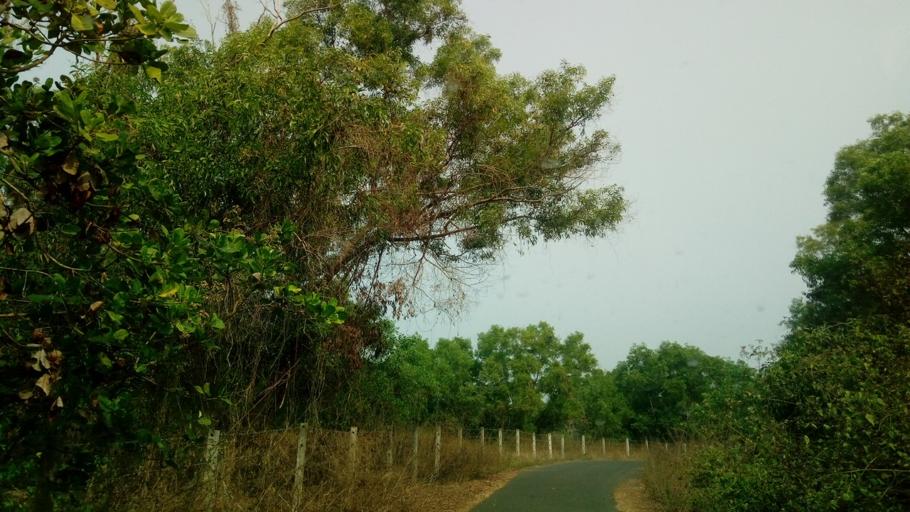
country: IN
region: Goa
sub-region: South Goa
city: Varca
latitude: 15.2179
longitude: 73.9340
